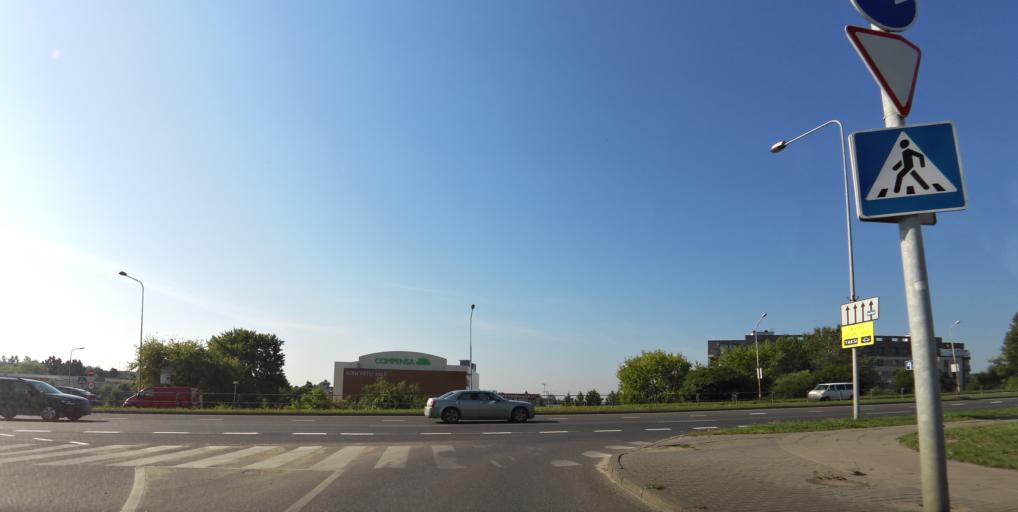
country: LT
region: Vilnius County
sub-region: Vilnius
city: Vilnius
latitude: 54.7133
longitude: 25.2764
